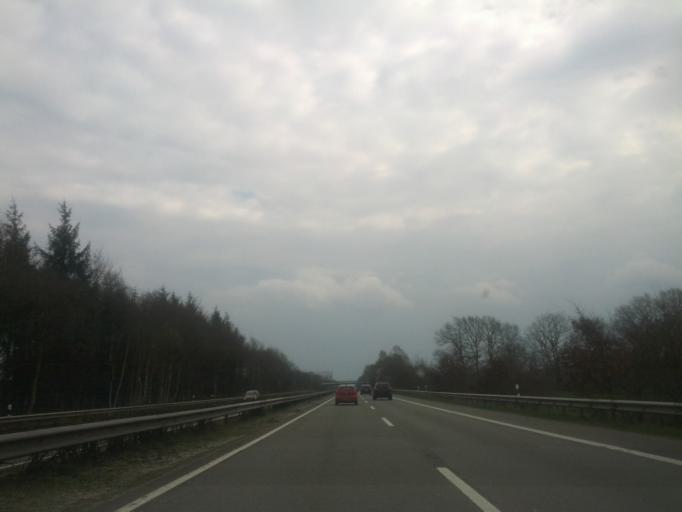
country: DE
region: Lower Saxony
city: Westerstede
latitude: 53.2725
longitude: 7.9199
